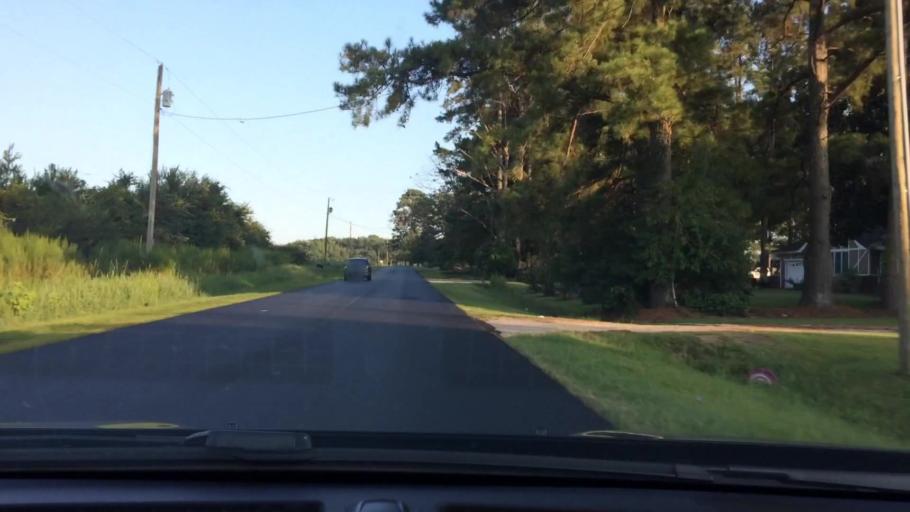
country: US
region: North Carolina
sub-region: Pitt County
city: Ayden
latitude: 35.4499
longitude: -77.4643
